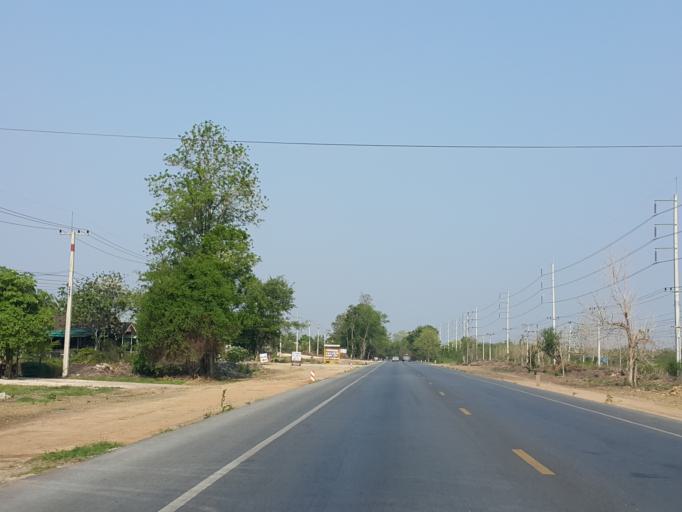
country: TH
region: Kanchanaburi
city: Sai Yok
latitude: 14.0894
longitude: 99.3181
